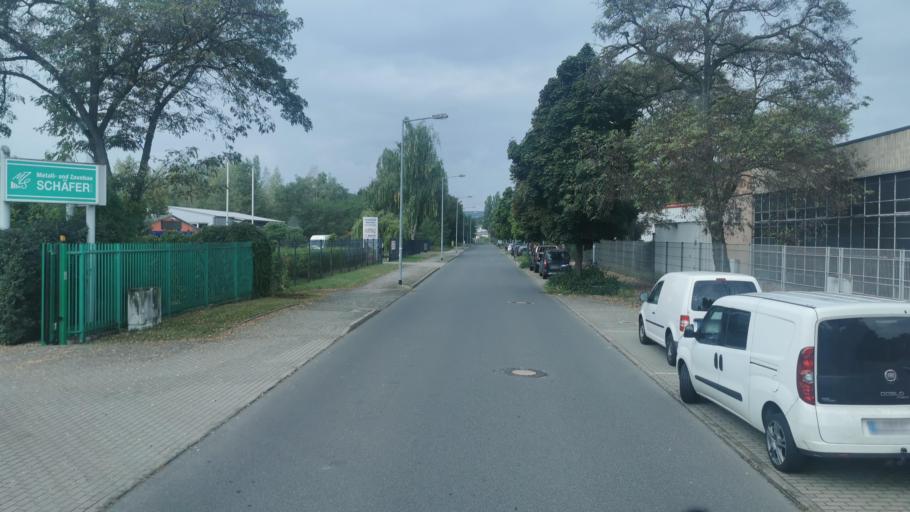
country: DE
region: Brandenburg
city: Eisenhuettenstadt
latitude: 52.1572
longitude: 14.6271
